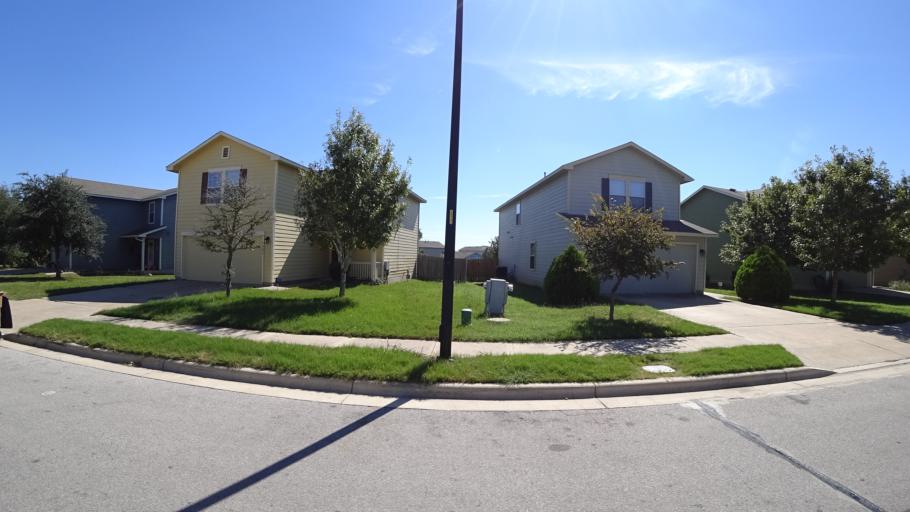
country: US
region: Texas
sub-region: Travis County
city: Austin
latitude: 30.2009
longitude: -97.6943
